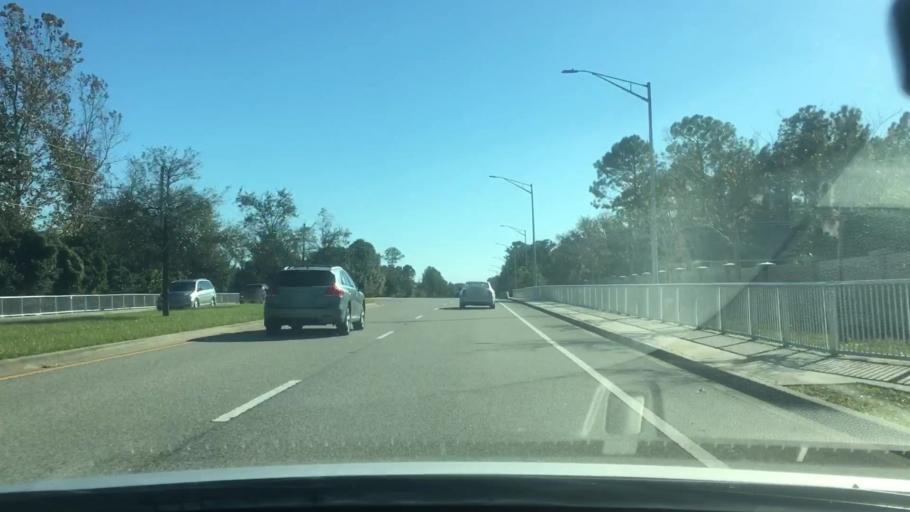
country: US
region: Florida
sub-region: Duval County
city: Neptune Beach
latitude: 30.3075
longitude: -81.4593
